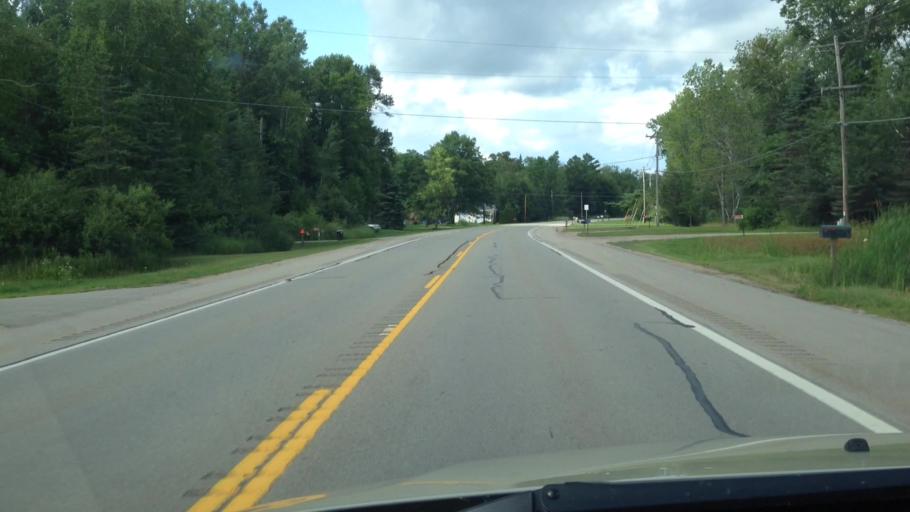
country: US
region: Michigan
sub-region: Menominee County
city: Menominee
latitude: 45.1614
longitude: -87.5903
